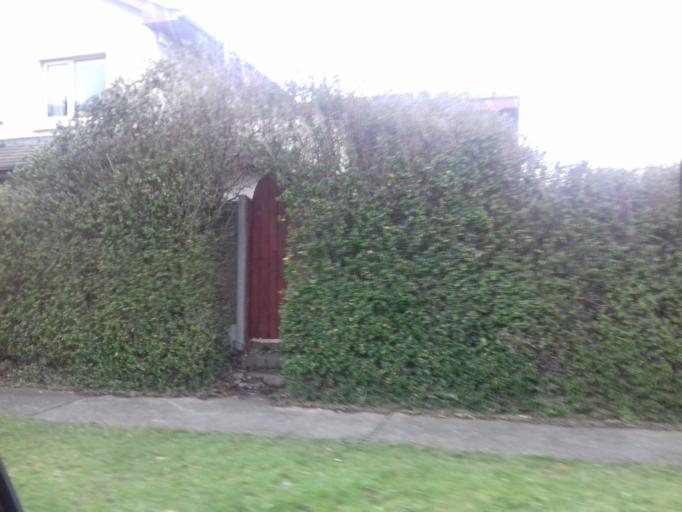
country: IE
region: Leinster
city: Portmarnock
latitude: 53.4373
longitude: -6.1297
